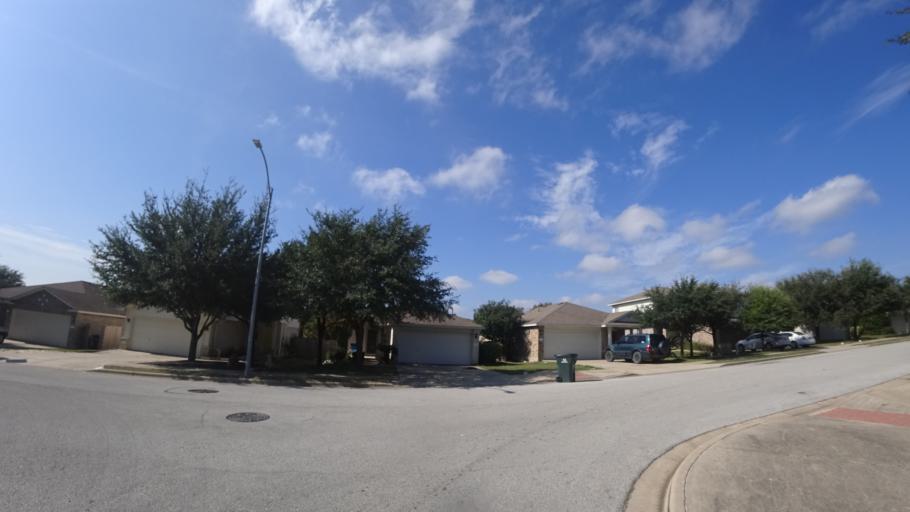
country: US
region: Texas
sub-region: Travis County
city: Pflugerville
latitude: 30.4207
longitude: -97.6382
